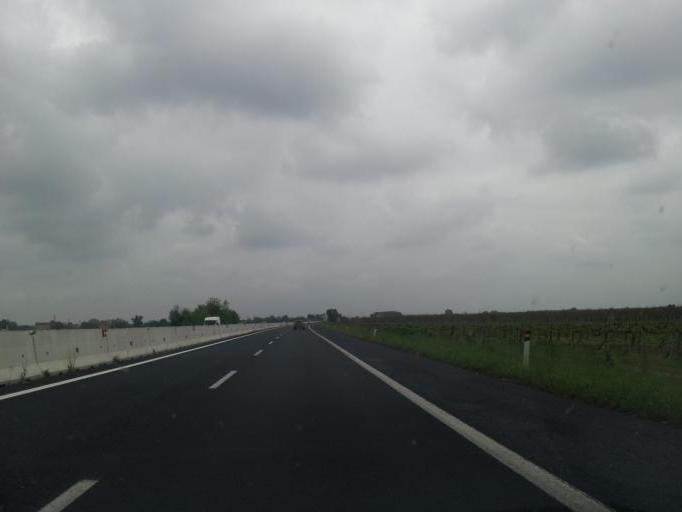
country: IT
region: Veneto
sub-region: Provincia di Treviso
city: Chiarano
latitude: 45.6955
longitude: 12.5820
